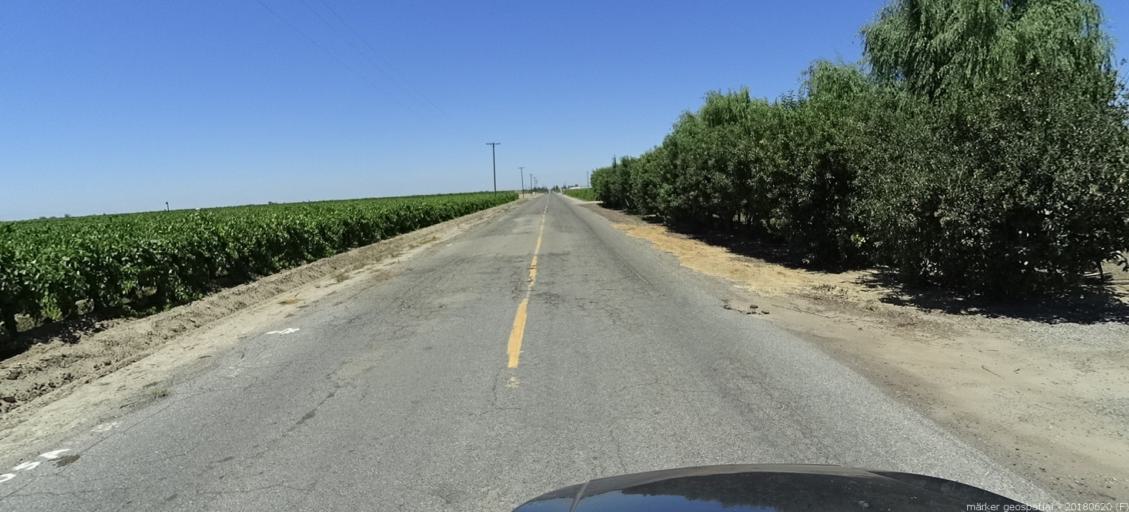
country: US
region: California
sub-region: Madera County
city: Parkwood
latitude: 36.8658
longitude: -120.0387
